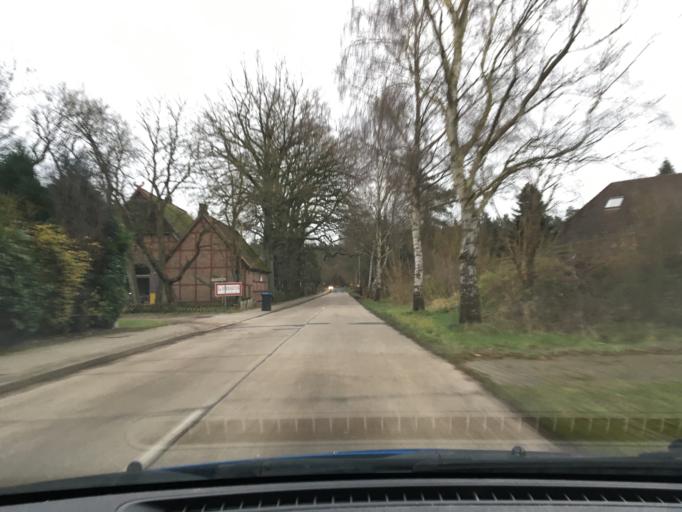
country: DE
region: Lower Saxony
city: Bleckede
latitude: 53.2809
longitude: 10.7565
